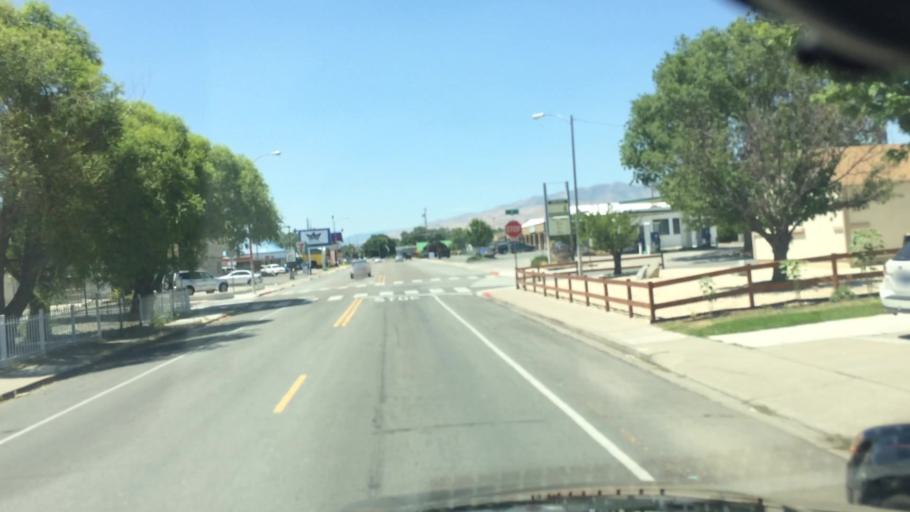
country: US
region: Nevada
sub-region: Washoe County
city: Sparks
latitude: 39.5474
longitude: -119.7477
